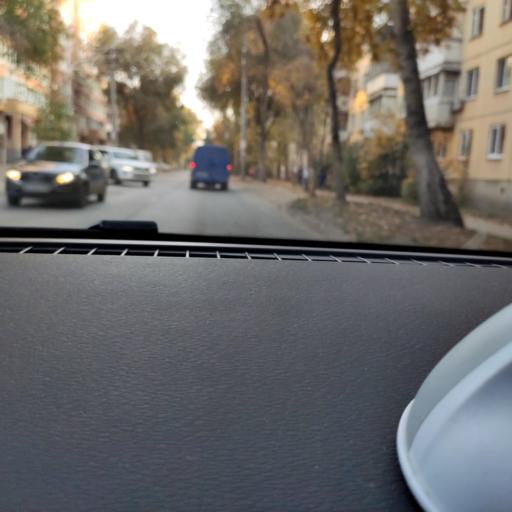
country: RU
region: Samara
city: Samara
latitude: 53.1953
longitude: 50.1838
